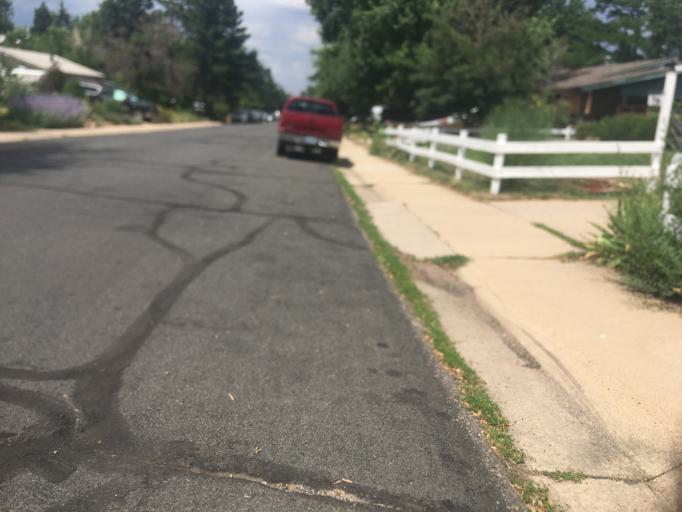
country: US
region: Colorado
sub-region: Boulder County
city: Boulder
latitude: 39.9829
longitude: -105.2436
